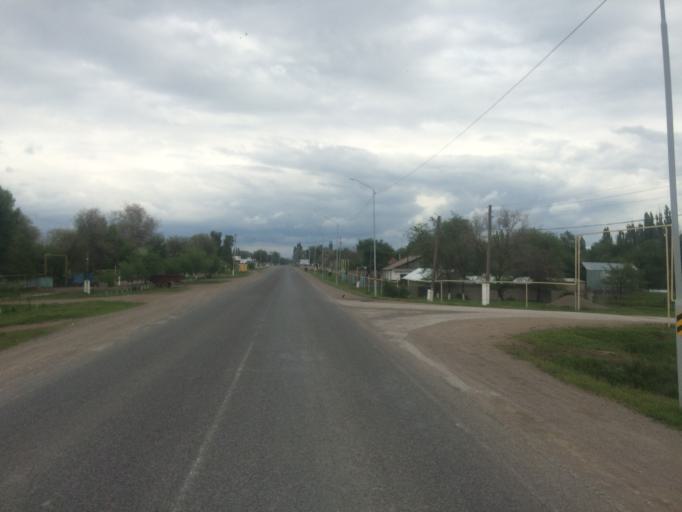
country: KZ
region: Zhambyl
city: Georgiyevka
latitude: 43.2278
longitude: 74.3886
